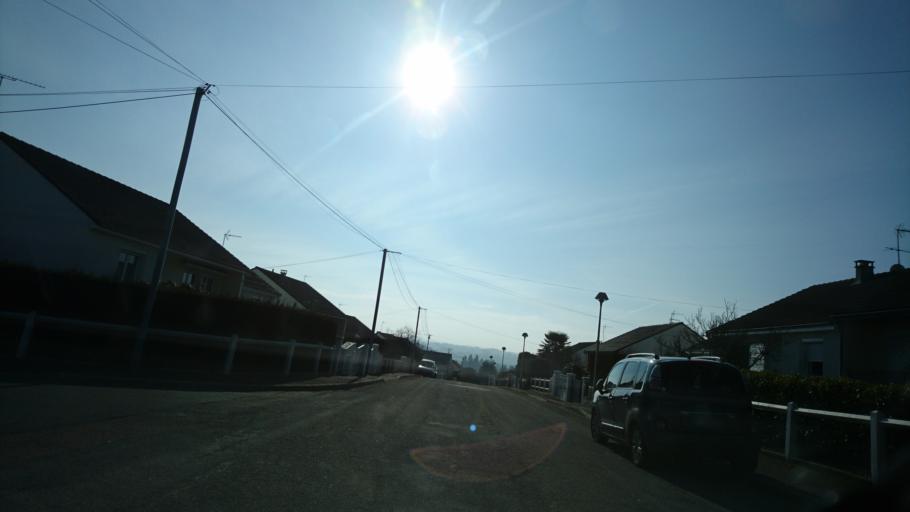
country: FR
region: Limousin
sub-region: Departement de la Haute-Vienne
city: Le Palais-sur-Vienne
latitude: 45.8713
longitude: 1.3144
